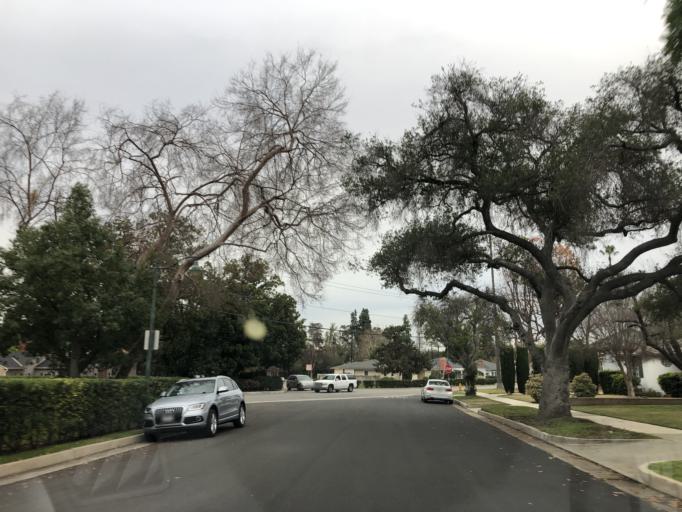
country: US
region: California
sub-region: Los Angeles County
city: San Marino
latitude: 34.1155
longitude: -118.0985
